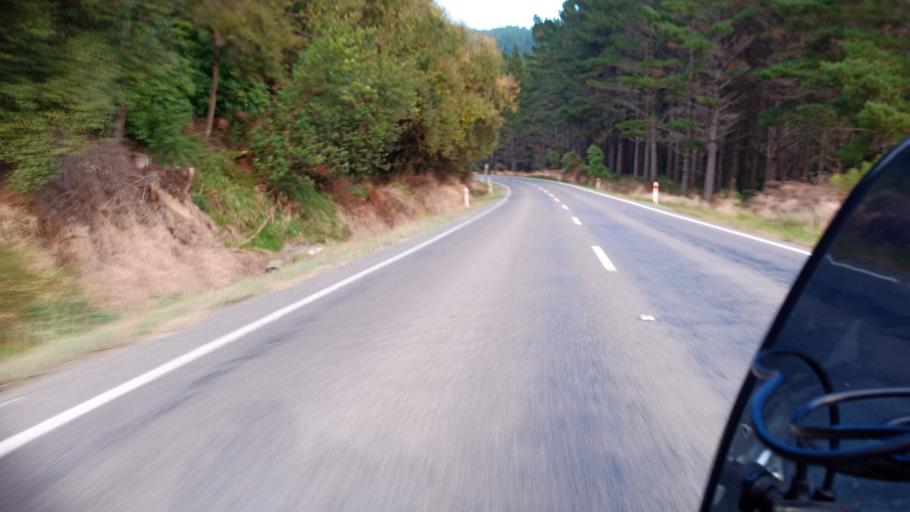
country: NZ
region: Gisborne
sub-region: Gisborne District
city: Gisborne
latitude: -38.8301
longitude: 177.8984
